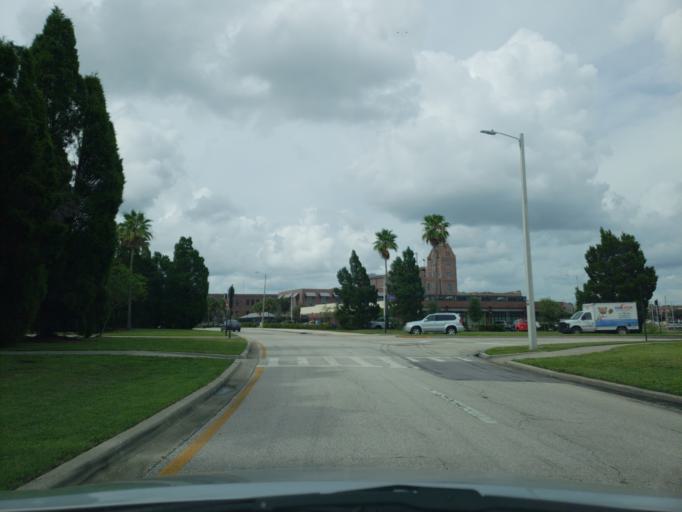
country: US
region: Florida
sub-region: Hillsborough County
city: Tampa
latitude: 27.9576
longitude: -82.4471
